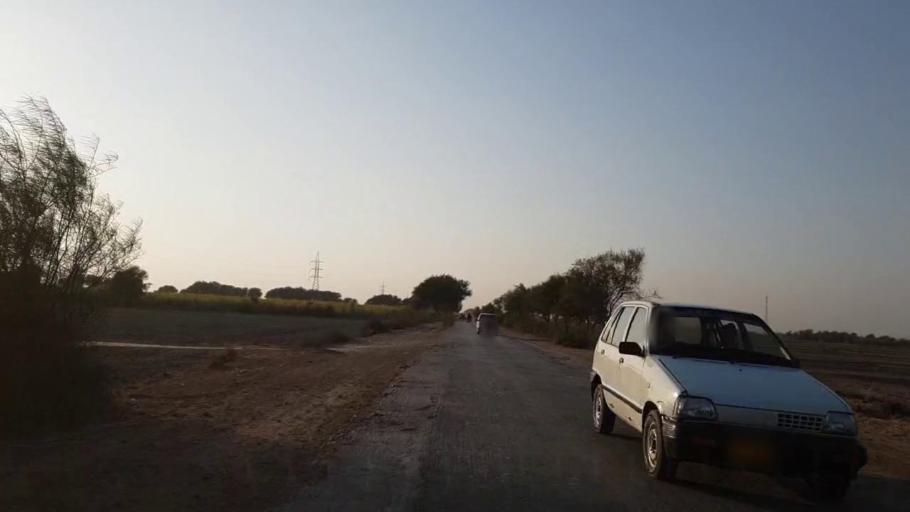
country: PK
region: Sindh
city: Chambar
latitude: 25.2180
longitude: 68.7529
